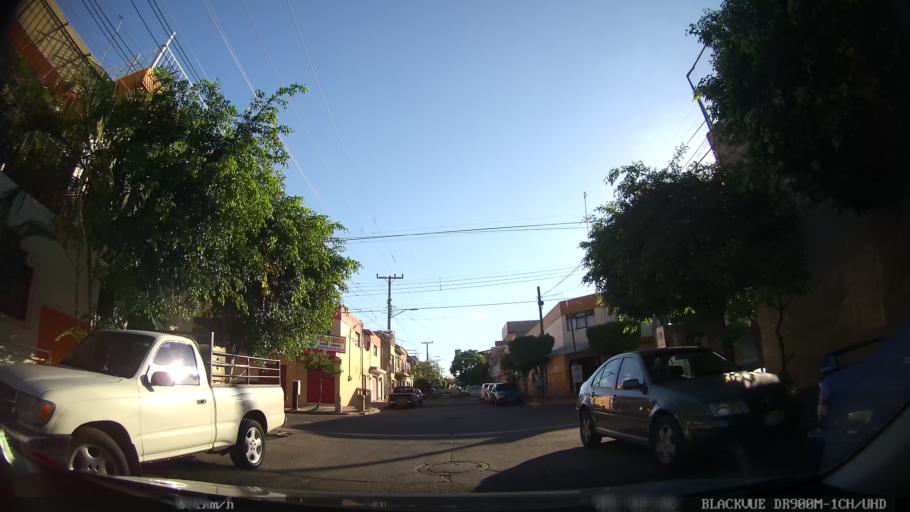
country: MX
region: Jalisco
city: Tlaquepaque
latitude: 20.7017
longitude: -103.2921
